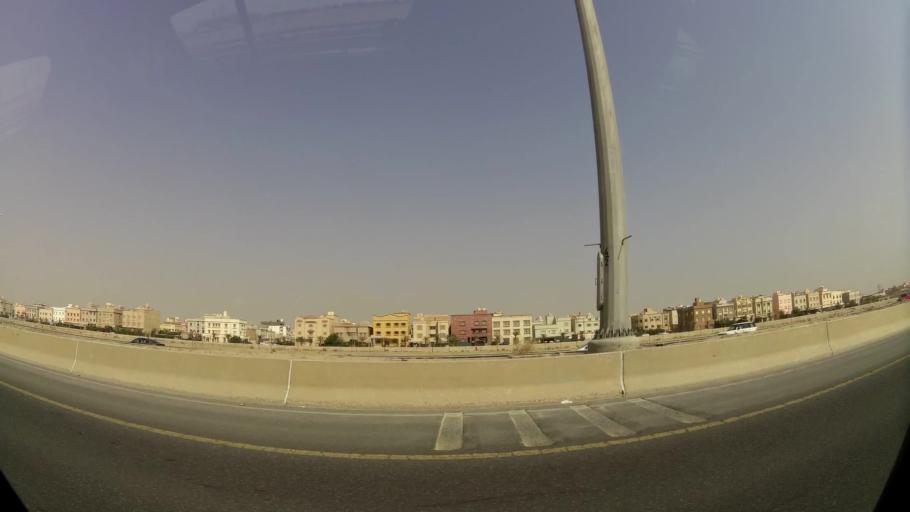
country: KW
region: Muhafazat al Jahra'
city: Al Jahra'
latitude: 29.2999
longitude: 47.6996
